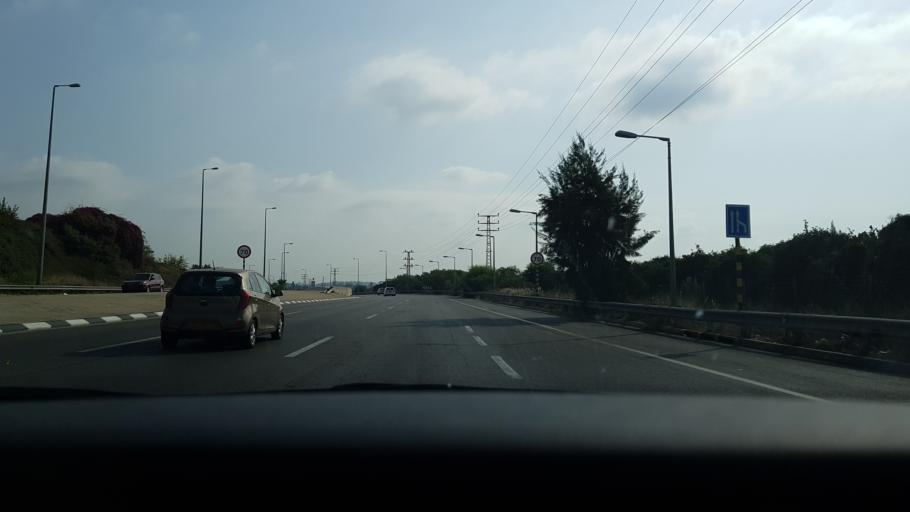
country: IL
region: Central District
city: Ness Ziona
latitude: 31.9212
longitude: 34.7799
